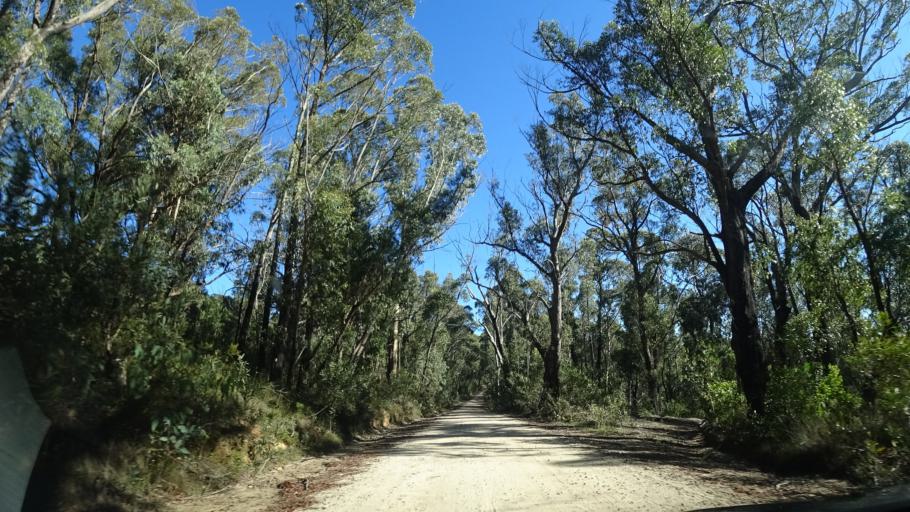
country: AU
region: New South Wales
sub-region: Lithgow
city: Lithgow
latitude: -33.4937
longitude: 150.2684
